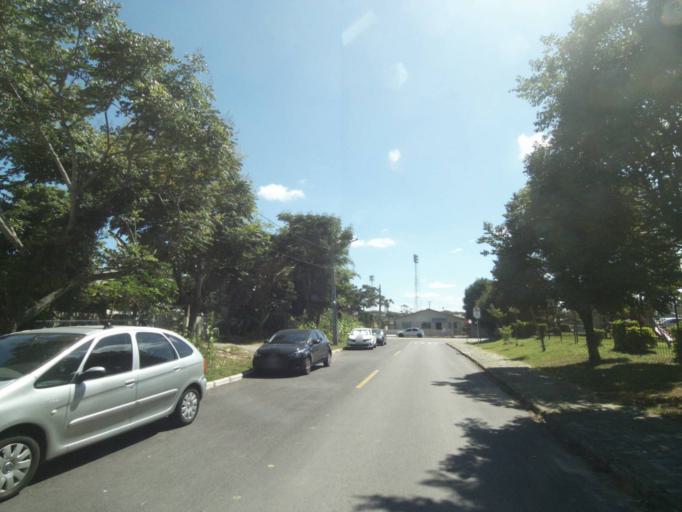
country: BR
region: Parana
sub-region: Pinhais
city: Pinhais
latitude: -25.4342
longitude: -49.2194
